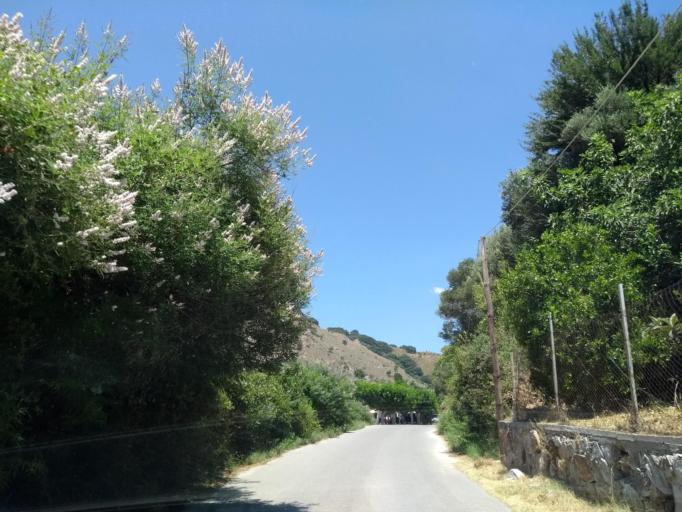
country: GR
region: Crete
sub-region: Nomos Chanias
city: Georgioupolis
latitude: 35.3341
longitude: 24.2778
